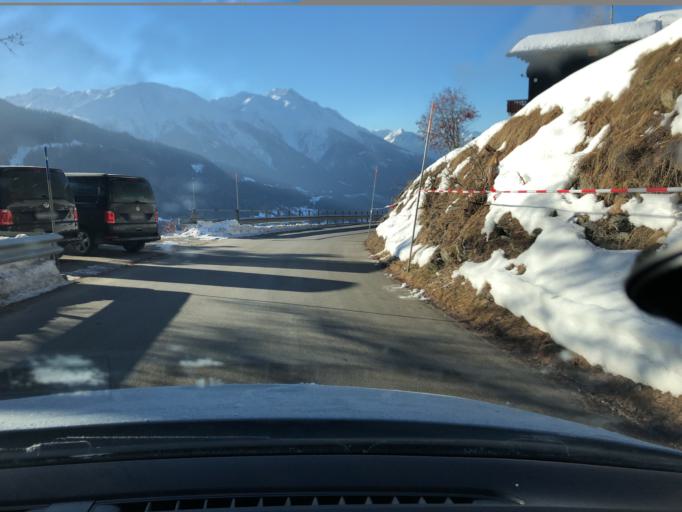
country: CH
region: Valais
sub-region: Goms District
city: Fiesch
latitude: 46.4265
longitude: 8.1660
